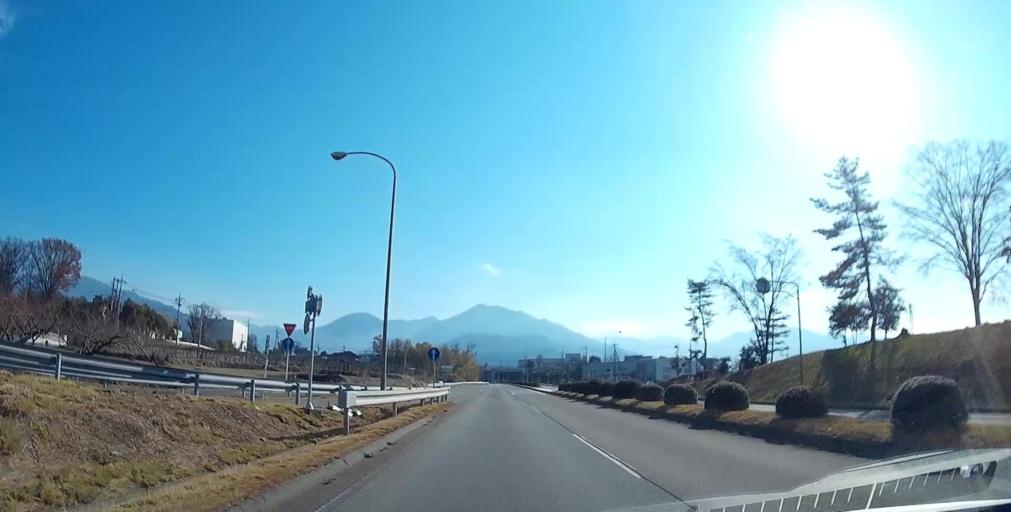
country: JP
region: Yamanashi
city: Isawa
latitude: 35.6367
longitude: 138.6729
